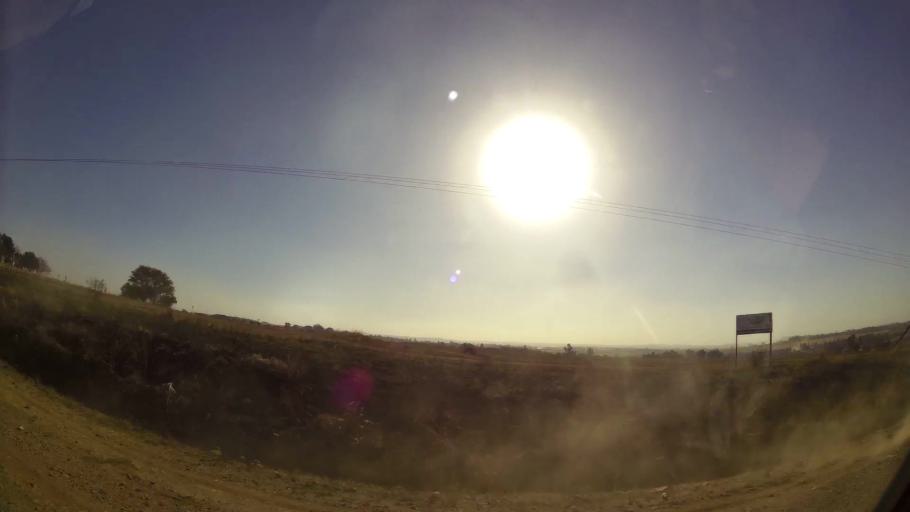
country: ZA
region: Gauteng
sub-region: City of Johannesburg Metropolitan Municipality
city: Diepsloot
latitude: -25.9582
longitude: 27.9580
